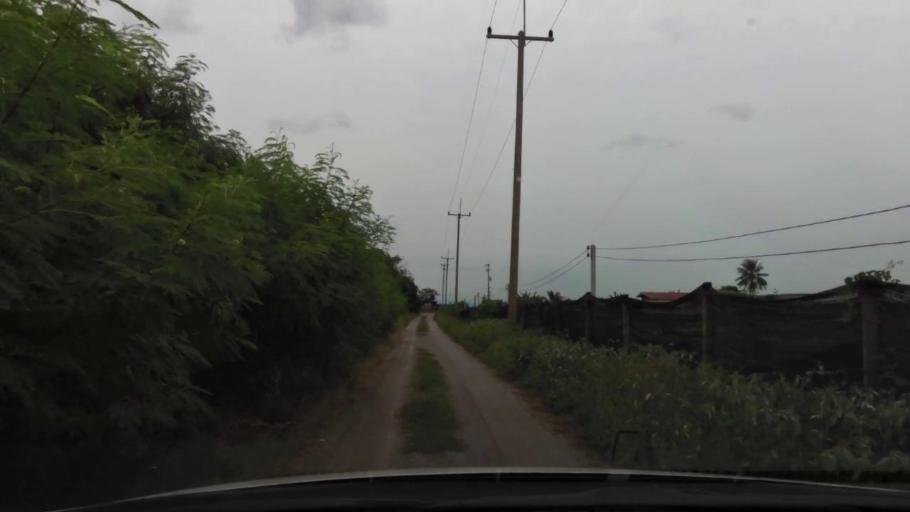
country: TH
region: Samut Sakhon
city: Ban Phaeo
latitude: 13.6147
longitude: 100.0297
